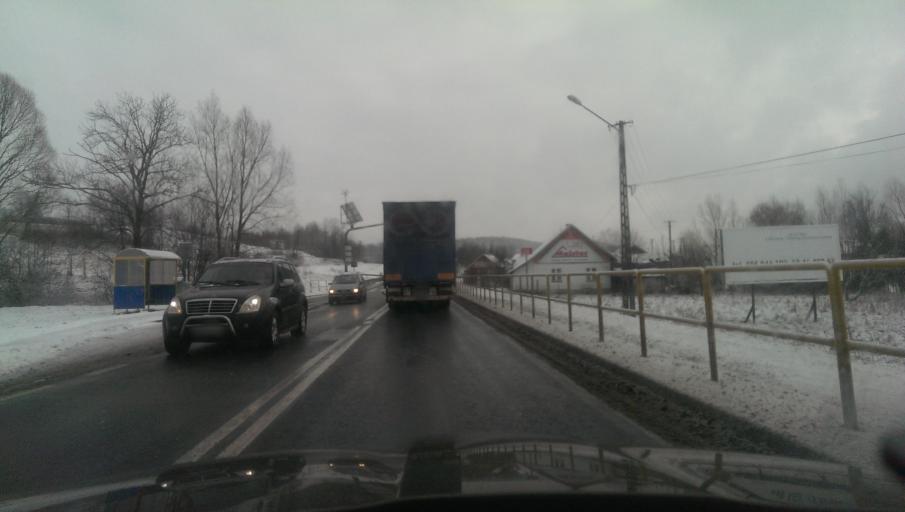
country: PL
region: Subcarpathian Voivodeship
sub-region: Powiat sanocki
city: Nowosielce-Gniewosz
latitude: 49.5583
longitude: 22.1051
